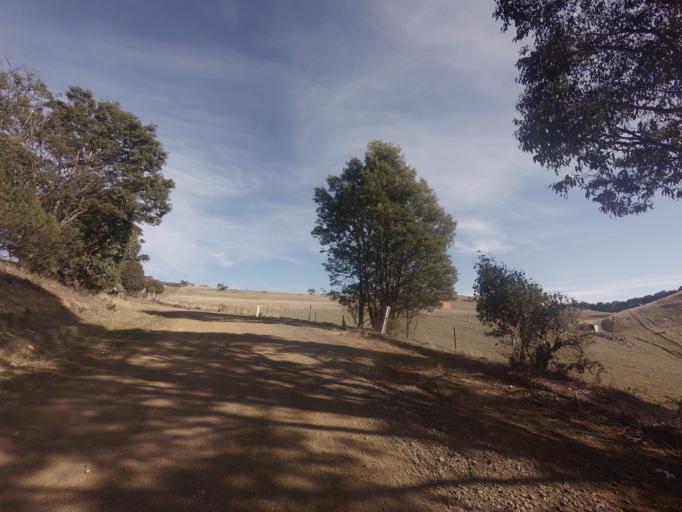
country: AU
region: Tasmania
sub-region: Sorell
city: Sorell
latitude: -42.4864
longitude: 147.4788
